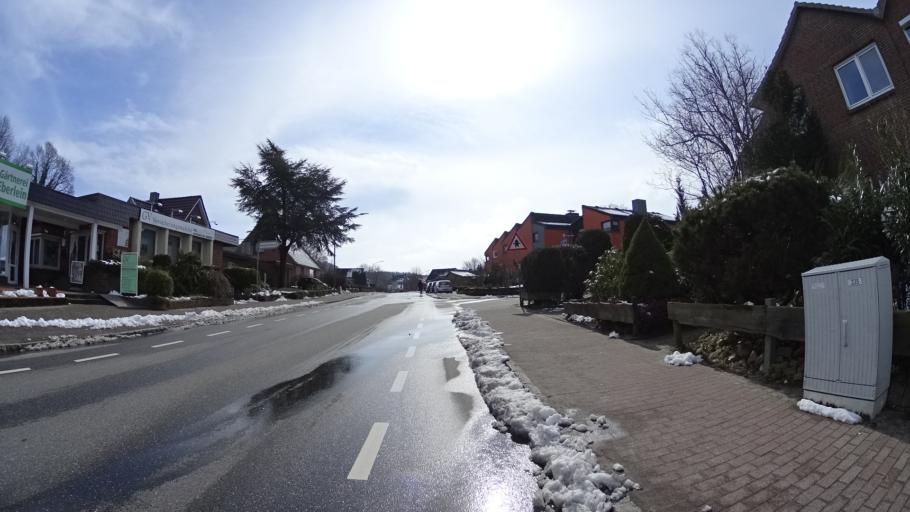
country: DE
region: Schleswig-Holstein
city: Boostedt
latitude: 54.0105
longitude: 10.0259
